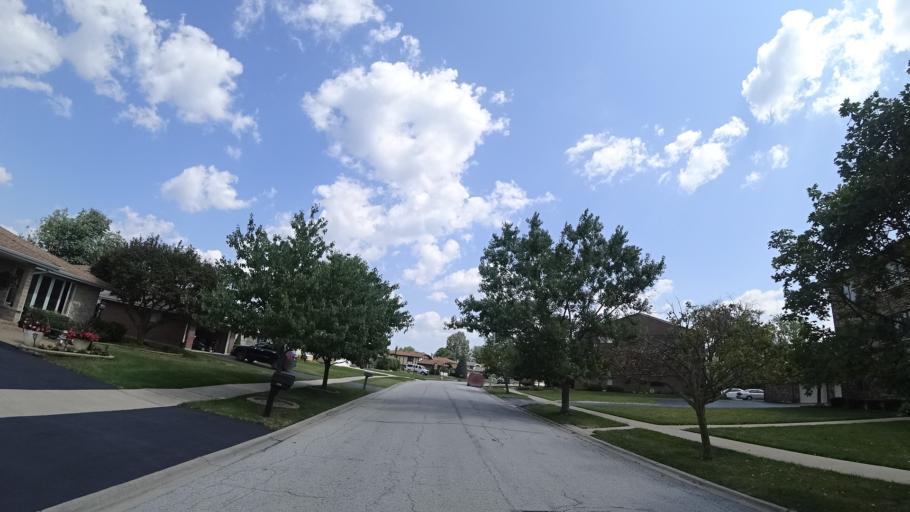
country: US
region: Illinois
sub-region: Cook County
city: Tinley Park
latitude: 41.6044
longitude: -87.8027
